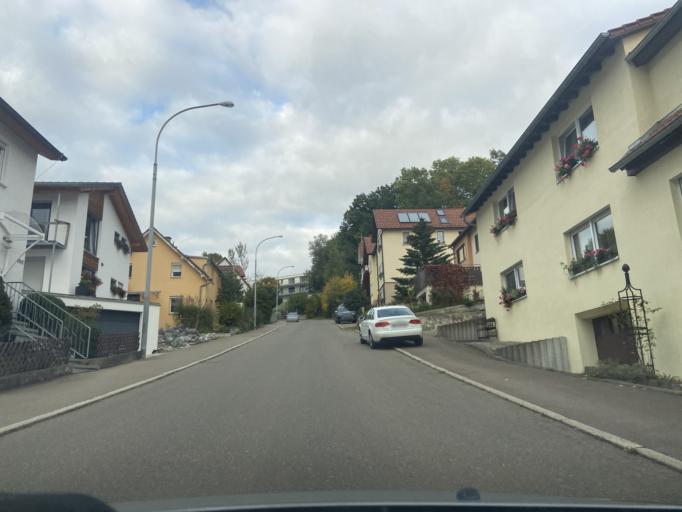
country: DE
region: Baden-Wuerttemberg
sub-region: Tuebingen Region
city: Sigmaringen
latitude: 48.0943
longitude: 9.2173
